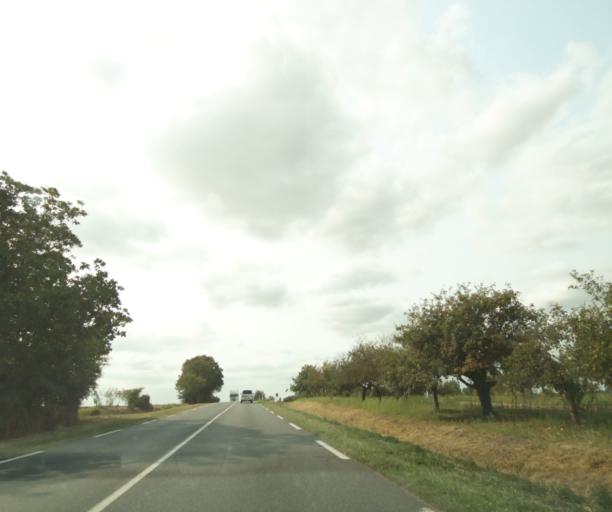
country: FR
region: Centre
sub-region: Departement de l'Indre
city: Clion
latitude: 46.9346
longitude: 1.2564
